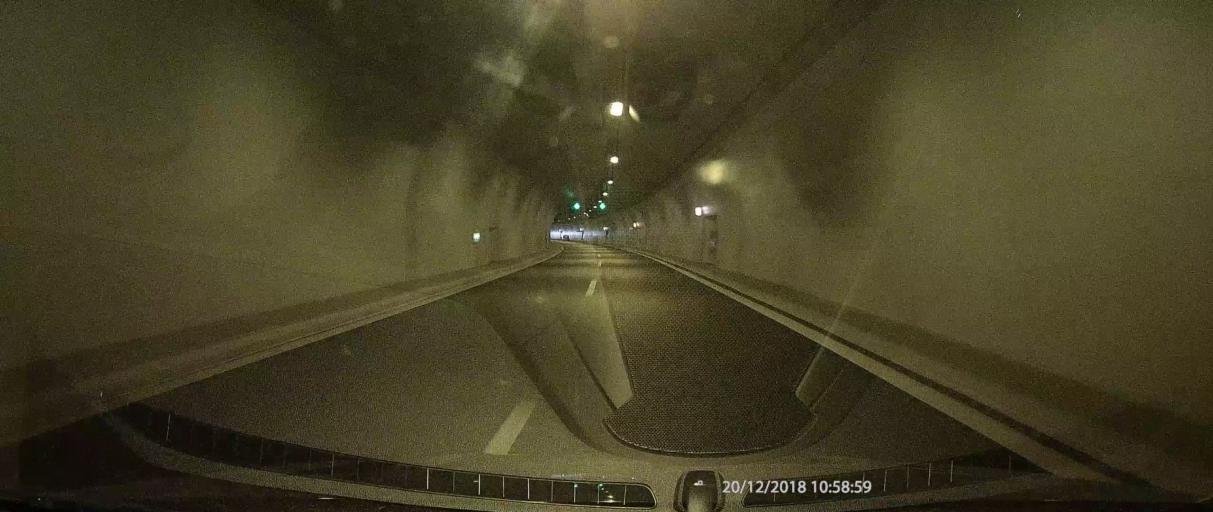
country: GR
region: Peloponnese
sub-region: Nomos Korinthias
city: Nemea
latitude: 37.6911
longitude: 22.5236
